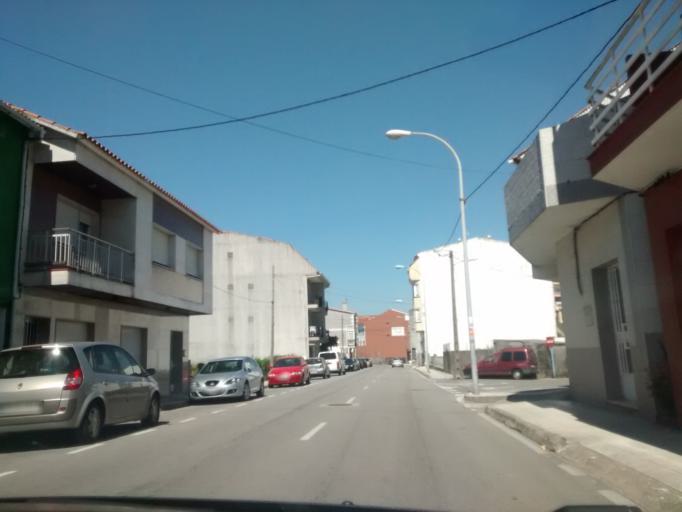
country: ES
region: Galicia
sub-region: Provincia de Pontevedra
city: O Grove
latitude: 42.4891
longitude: -8.8688
